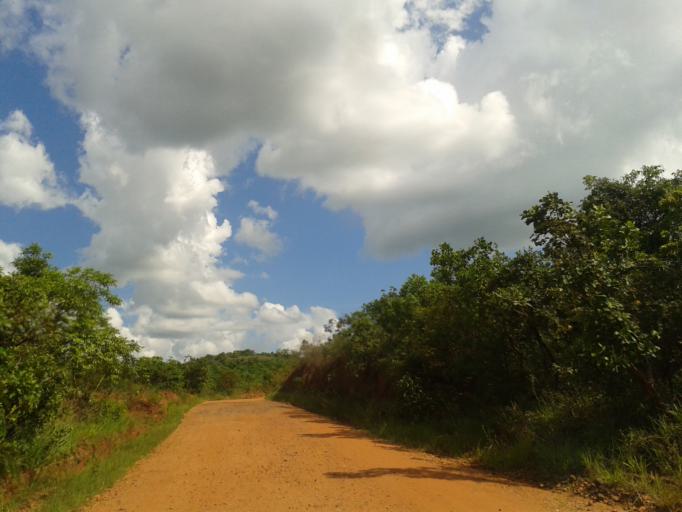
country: BR
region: Minas Gerais
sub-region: Campina Verde
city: Campina Verde
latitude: -19.3210
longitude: -49.8019
